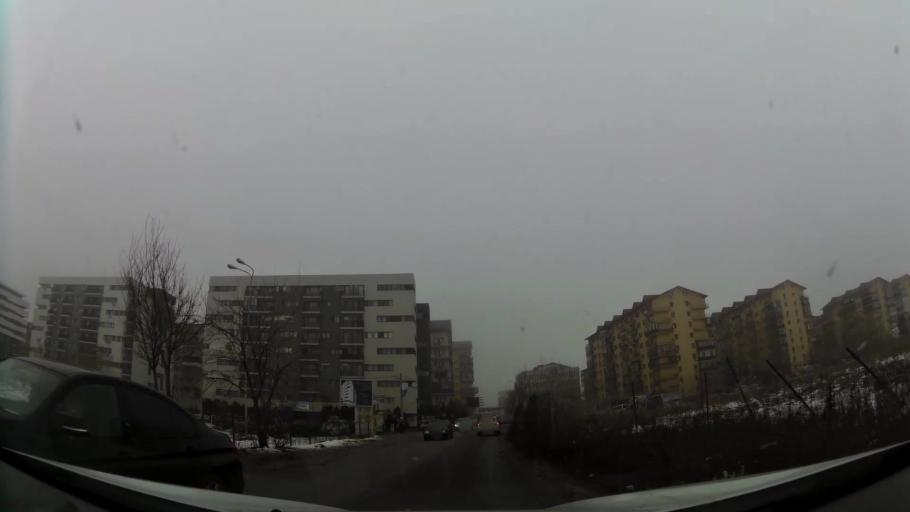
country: RO
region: Ilfov
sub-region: Comuna Chiajna
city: Chiajna
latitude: 44.4412
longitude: 25.9873
